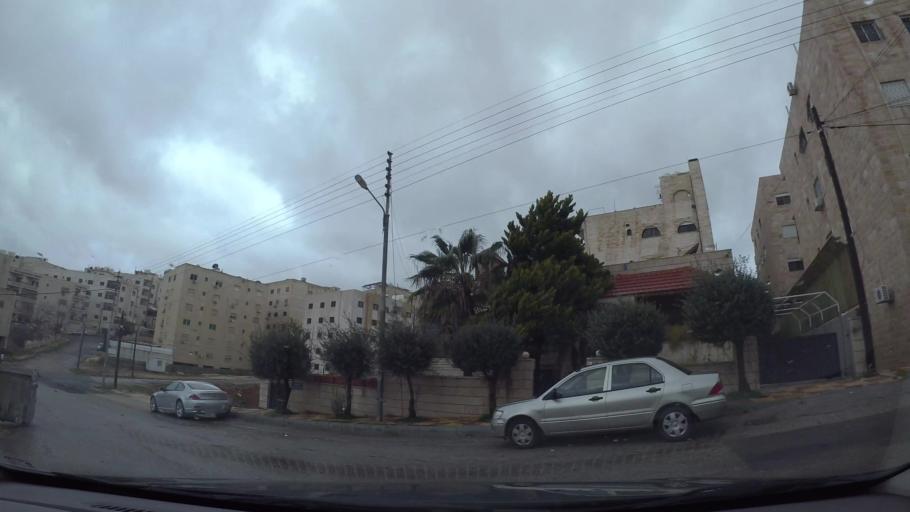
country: JO
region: Amman
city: Amman
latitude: 31.9968
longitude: 35.9244
